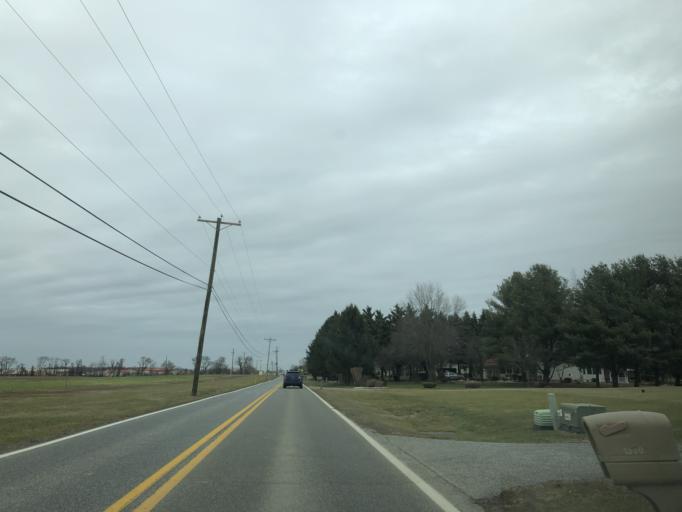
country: US
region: Delaware
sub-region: New Castle County
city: Middletown
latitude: 39.4946
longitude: -75.6886
